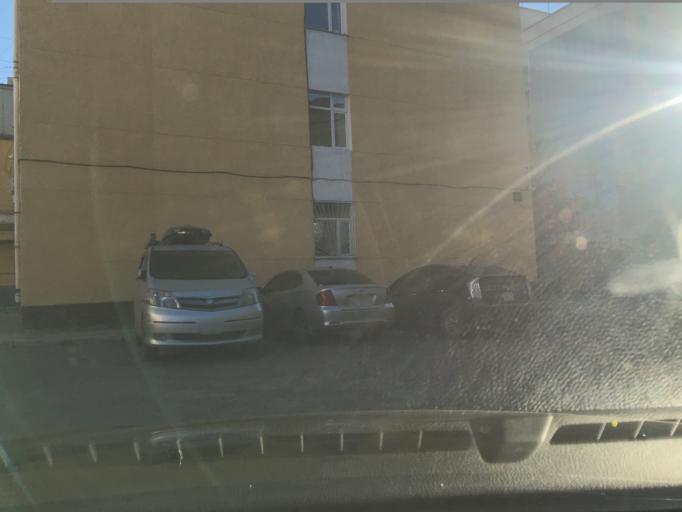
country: MN
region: Ulaanbaatar
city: Ulaanbaatar
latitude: 47.9236
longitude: 106.9130
